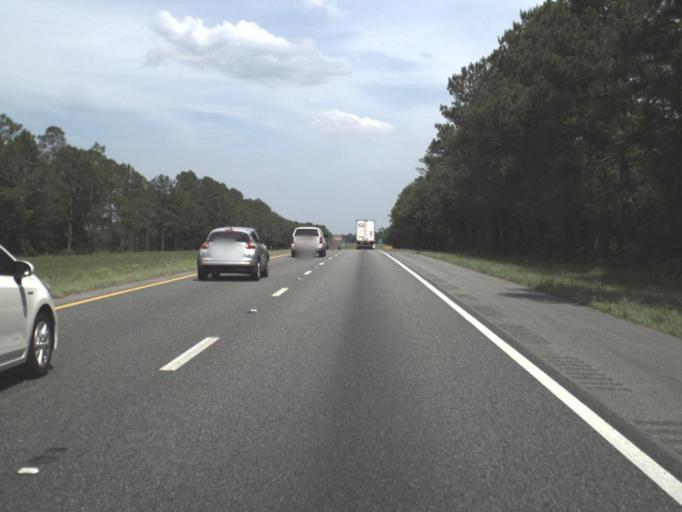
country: US
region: Florida
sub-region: Suwannee County
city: Live Oak
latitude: 30.3402
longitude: -83.1201
